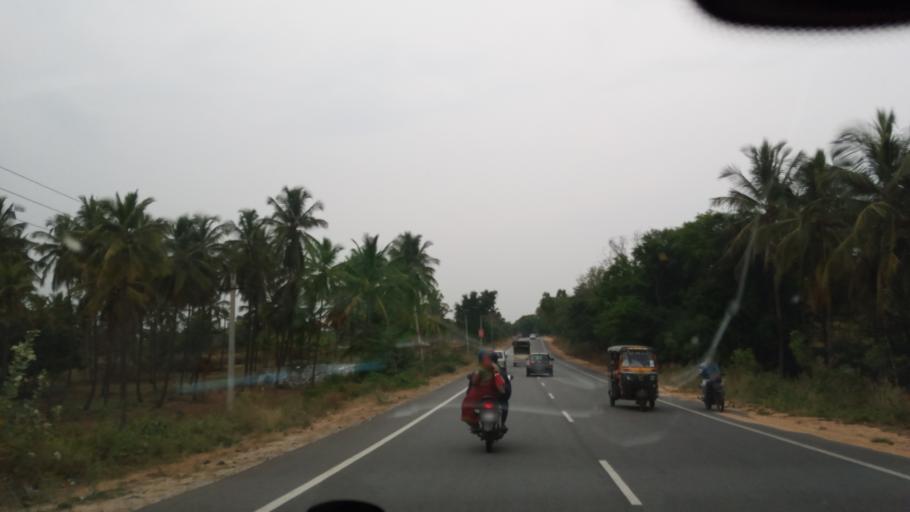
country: IN
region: Karnataka
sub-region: Mandya
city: Belluru
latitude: 12.9394
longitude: 76.7509
